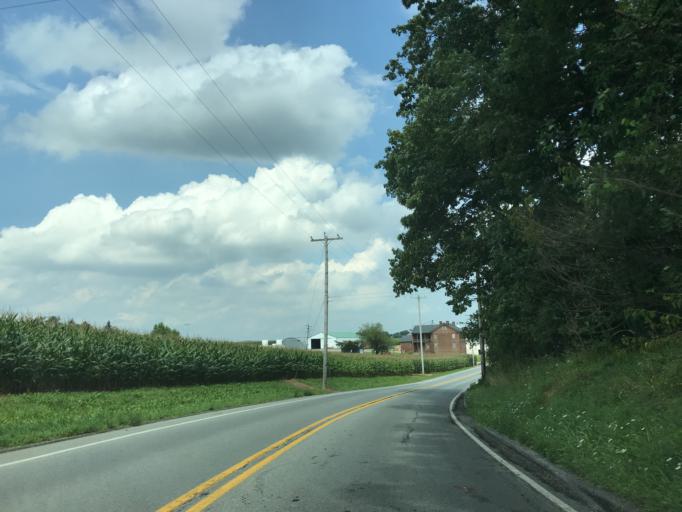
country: US
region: Pennsylvania
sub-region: York County
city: Red Lion
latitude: 39.8661
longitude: -76.6194
